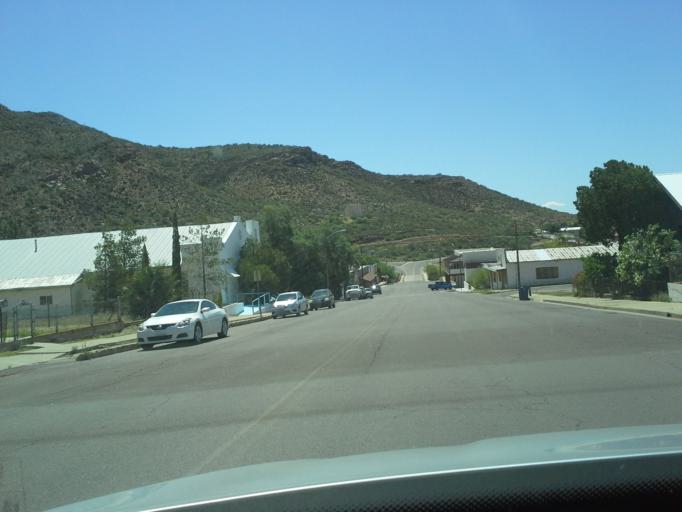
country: US
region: Arizona
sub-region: Pinal County
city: Superior
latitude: 33.2955
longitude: -111.0966
